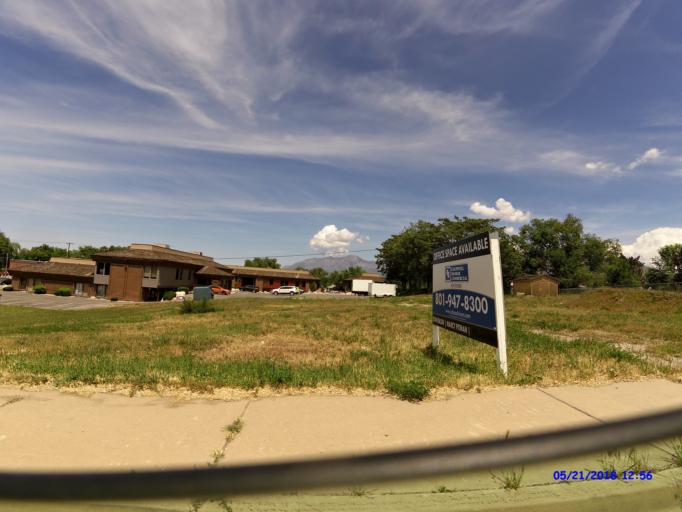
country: US
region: Utah
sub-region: Weber County
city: South Ogden
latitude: 41.1979
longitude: -111.9758
